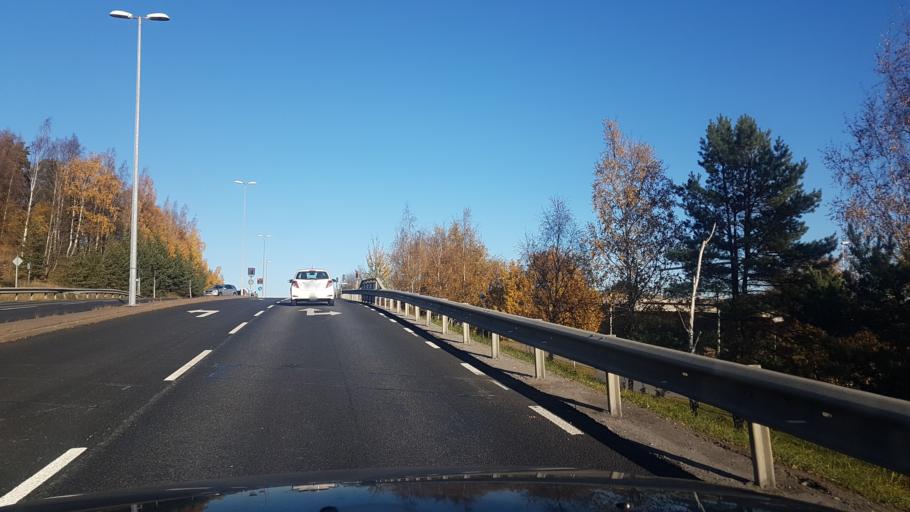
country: SE
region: Stockholm
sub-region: Sigtuna Kommun
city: Marsta
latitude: 59.6227
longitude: 17.8598
